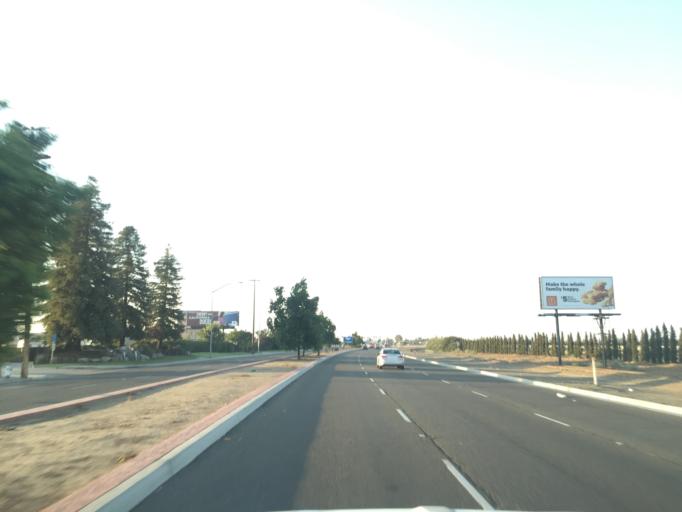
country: US
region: California
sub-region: Fresno County
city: Sunnyside
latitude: 36.7613
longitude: -119.7005
